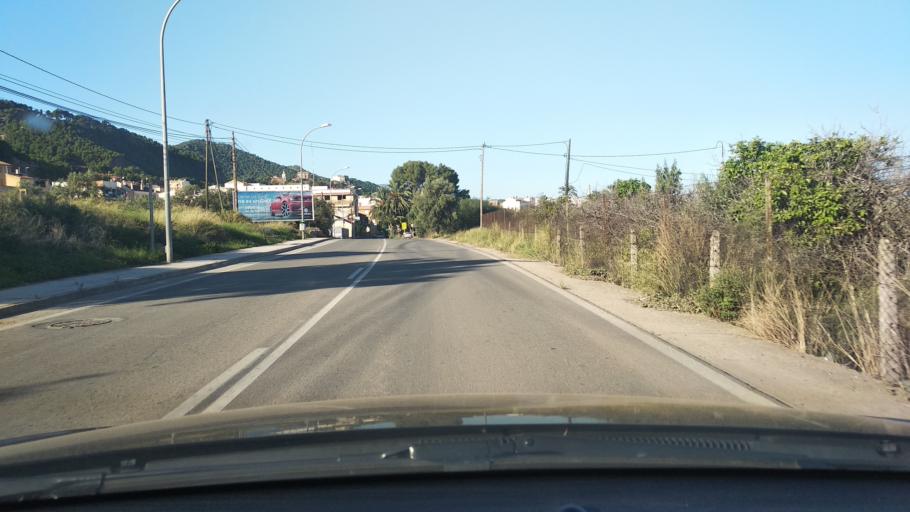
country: ES
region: Murcia
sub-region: Murcia
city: Murcia
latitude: 37.9470
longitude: -1.1065
